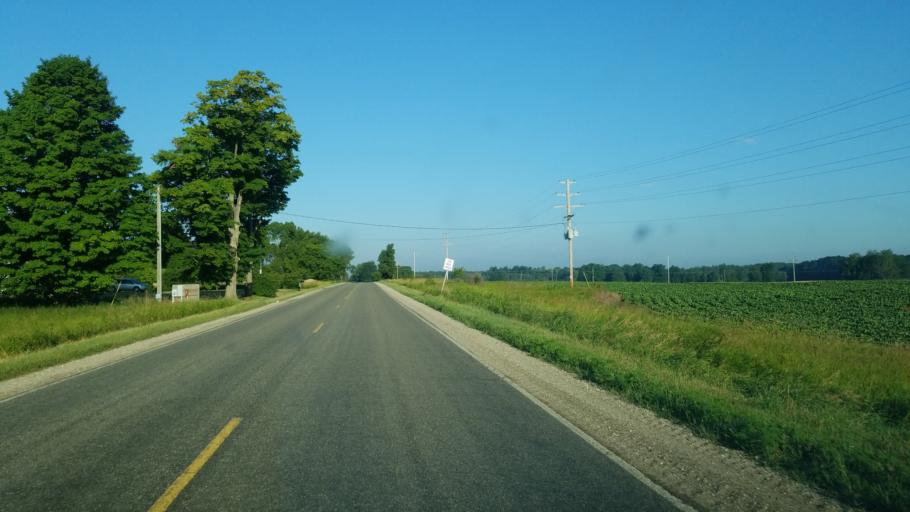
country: US
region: Michigan
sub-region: Mecosta County
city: Canadian Lakes
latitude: 43.5399
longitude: -85.2388
